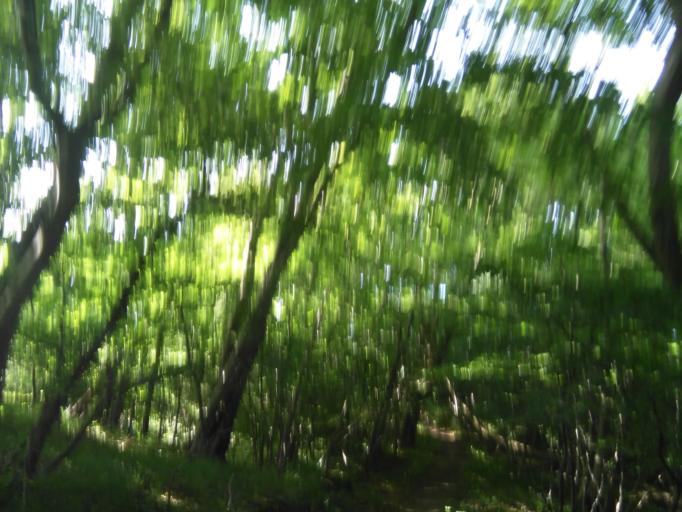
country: DK
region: Capital Region
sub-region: Bornholm Kommune
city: Akirkeby
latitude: 55.2252
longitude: 14.8794
